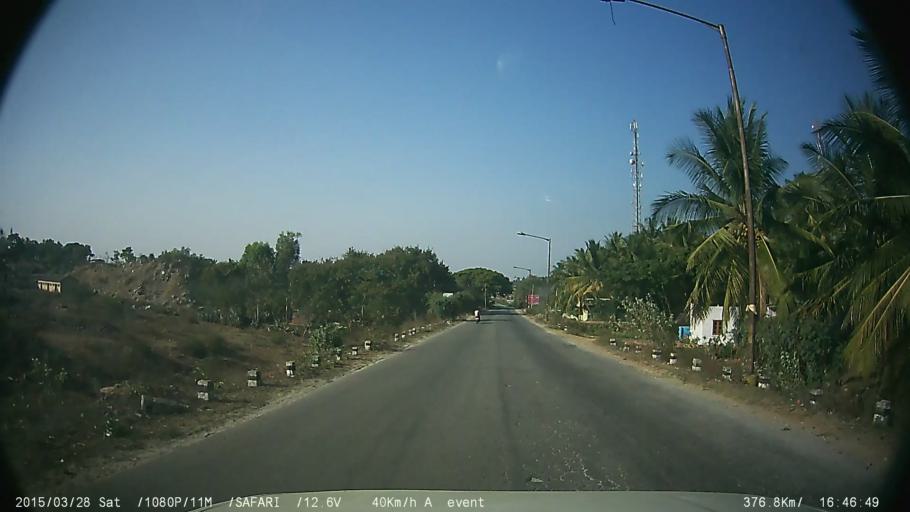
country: IN
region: Karnataka
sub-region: Mandya
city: Shrirangapattana
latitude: 12.4080
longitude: 76.5774
